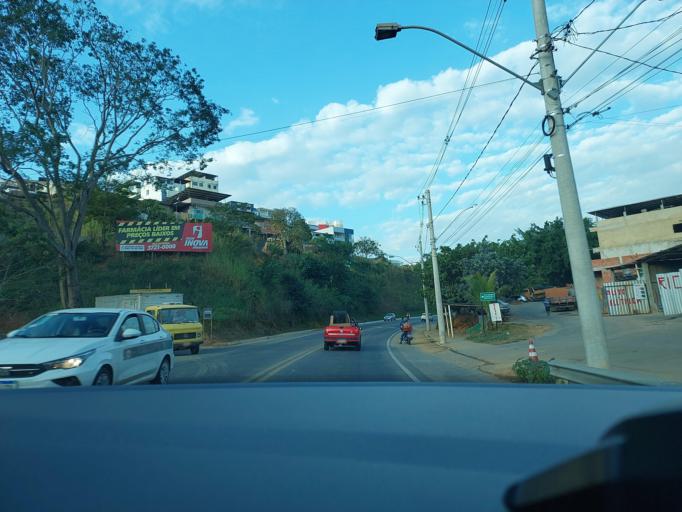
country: BR
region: Minas Gerais
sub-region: Muriae
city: Muriae
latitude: -21.1254
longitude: -42.3546
